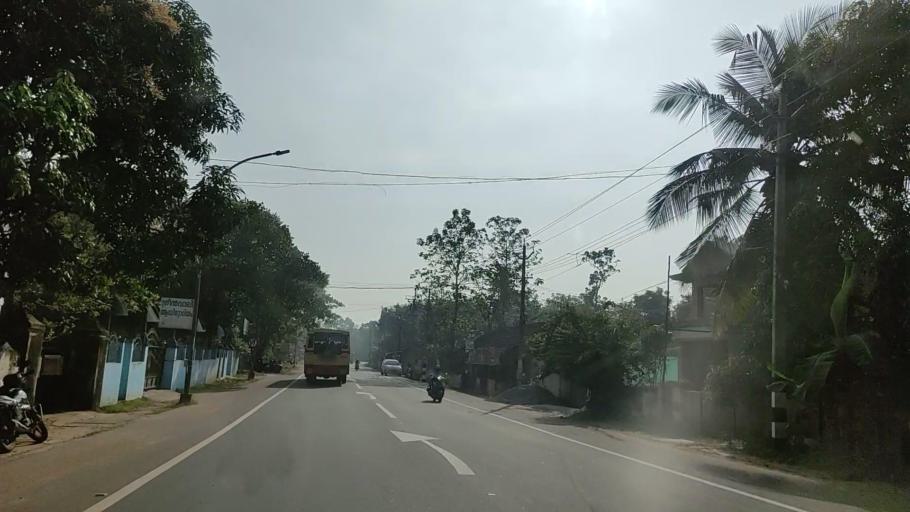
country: IN
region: Kerala
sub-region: Kollam
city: Punalur
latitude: 8.9843
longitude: 76.8055
